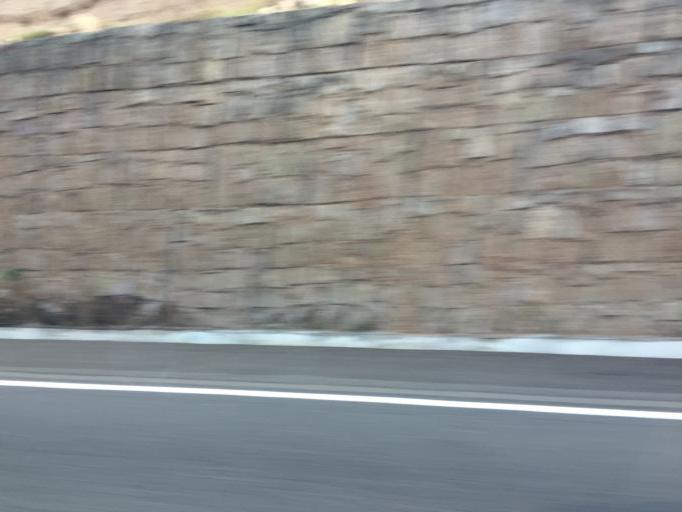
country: MX
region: Michoacan
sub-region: Cuitzeo
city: San Juan Benito Juarez (San Juan Tararameo)
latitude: 19.8932
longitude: -101.1597
